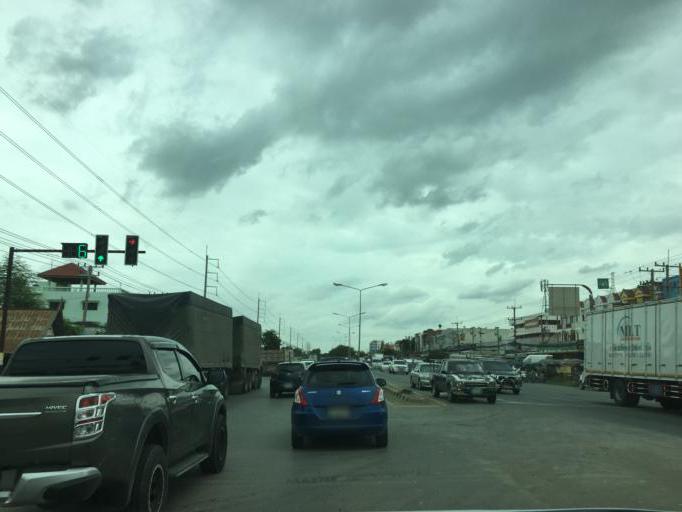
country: TH
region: Phra Nakhon Si Ayutthaya
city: Wang Noi
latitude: 14.2732
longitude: 100.6837
